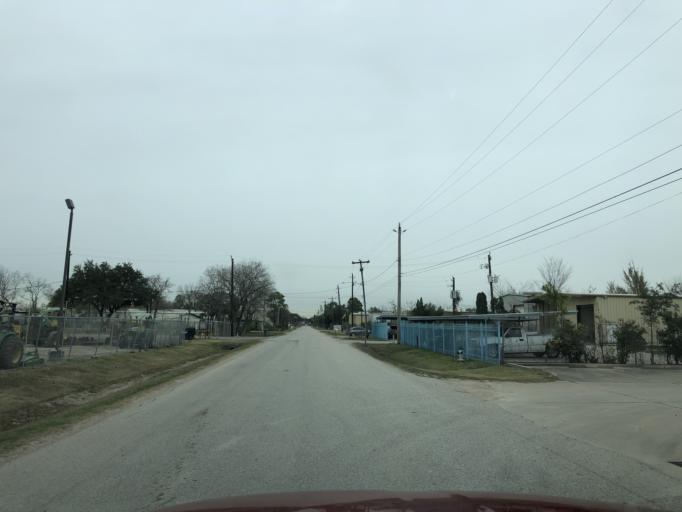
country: US
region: Texas
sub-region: Fort Bend County
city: Missouri City
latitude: 29.6320
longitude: -95.5223
